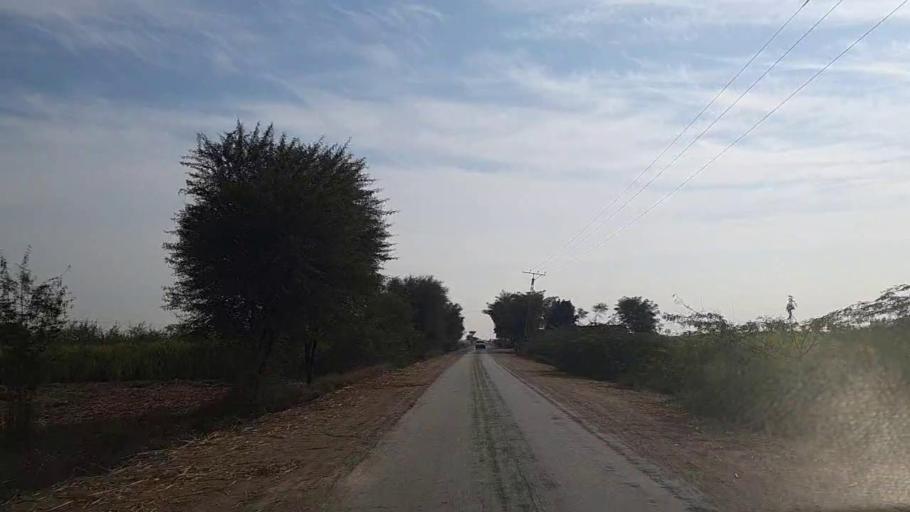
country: PK
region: Sindh
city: Daur
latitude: 26.4863
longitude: 68.4129
